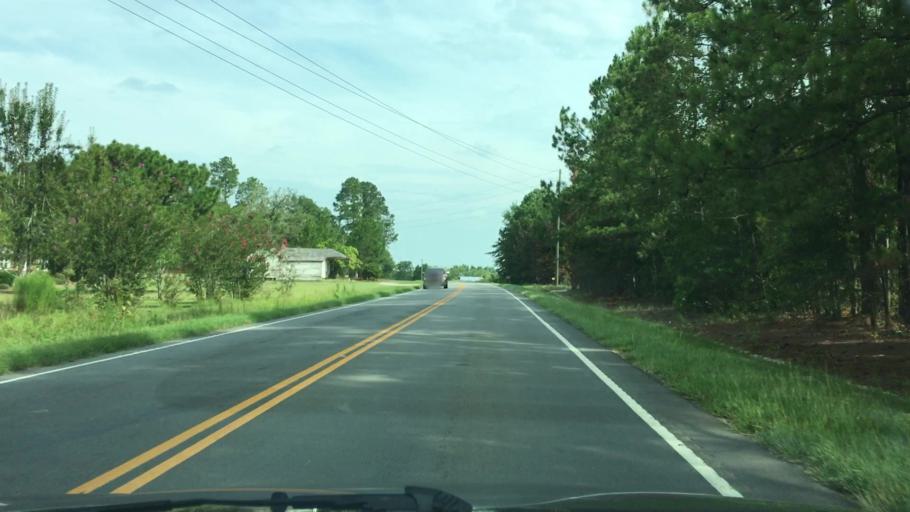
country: US
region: South Carolina
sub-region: Lexington County
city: Batesburg
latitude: 33.7402
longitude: -81.5162
